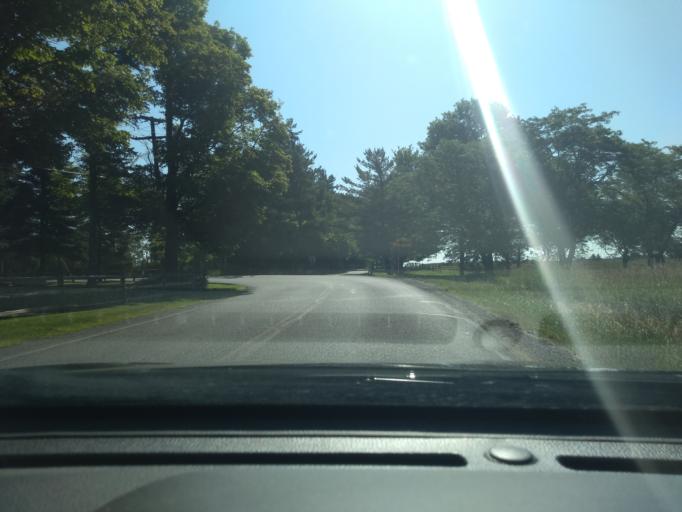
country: US
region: New York
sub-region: Erie County
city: Billington Heights
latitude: 42.7771
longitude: -78.6497
